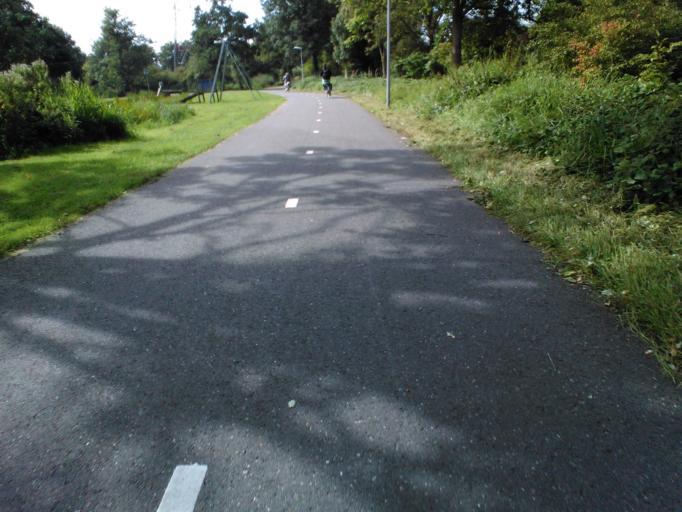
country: NL
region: South Holland
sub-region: Gemeente Voorschoten
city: Voorschoten
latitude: 52.1442
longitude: 4.4539
